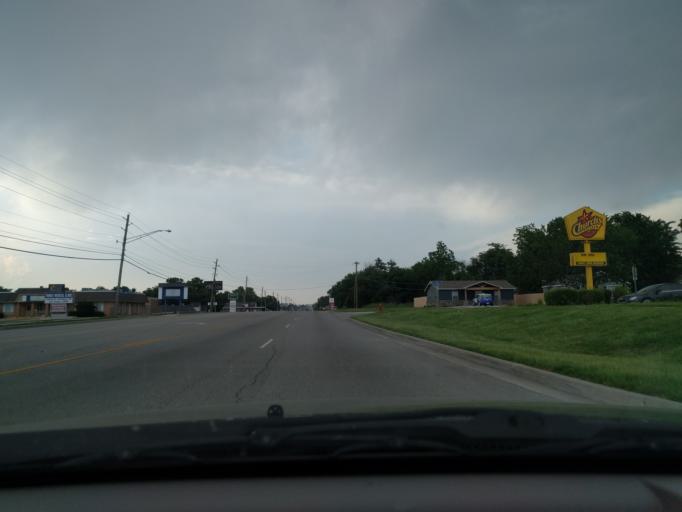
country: US
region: Oklahoma
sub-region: Tulsa County
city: Broken Arrow
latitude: 36.0479
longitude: -95.7974
